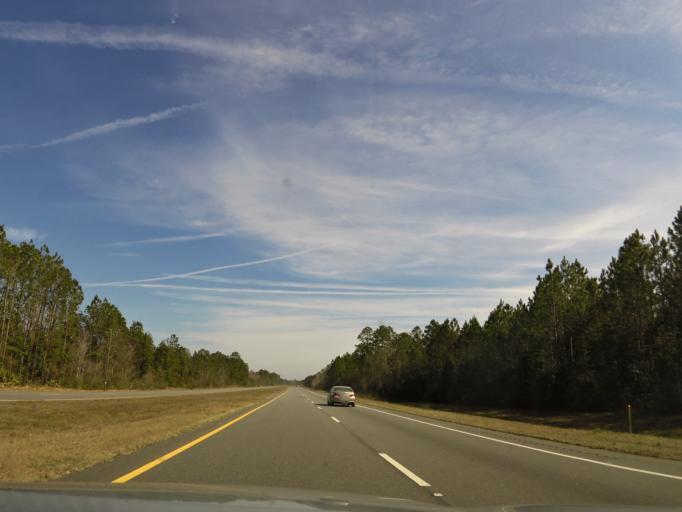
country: US
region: Georgia
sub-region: Brantley County
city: Nahunta
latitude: 31.2117
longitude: -81.9286
